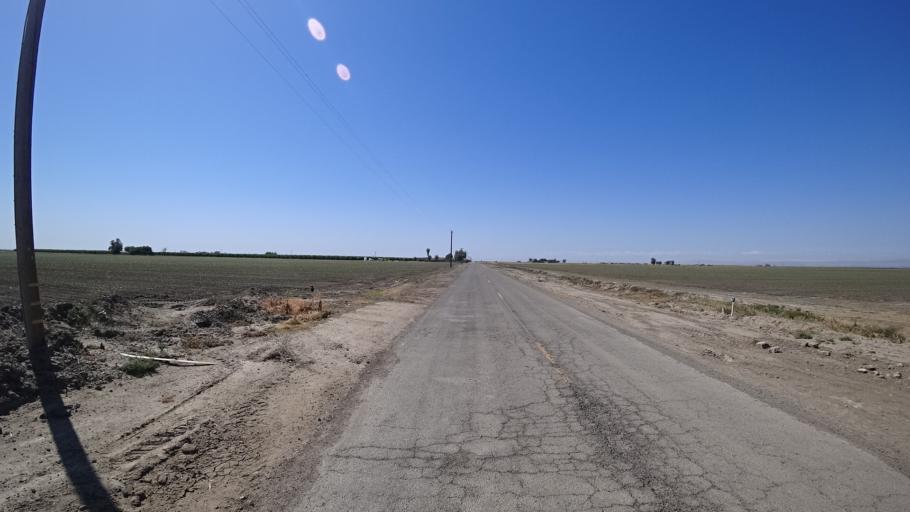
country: US
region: California
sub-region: Kings County
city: Stratford
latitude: 36.1710
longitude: -119.7802
